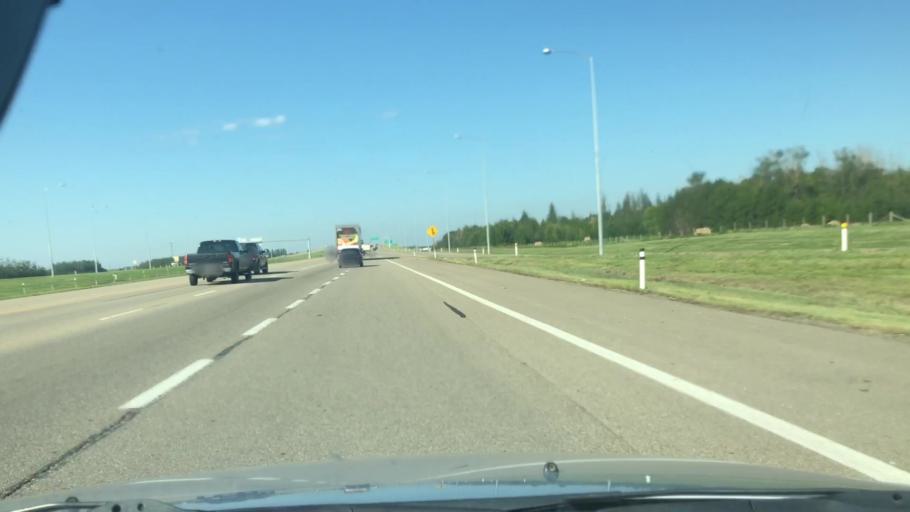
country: CA
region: Alberta
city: St. Albert
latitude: 53.6383
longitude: -113.5491
